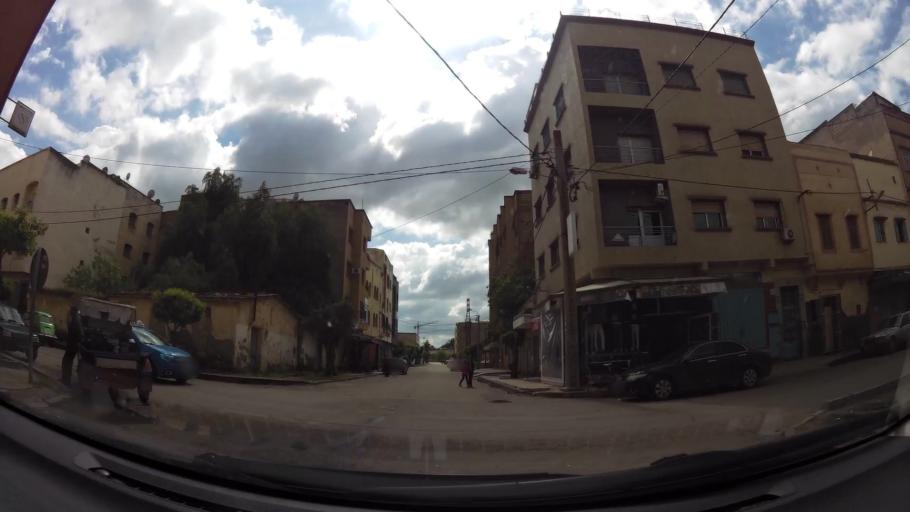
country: MA
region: Chaouia-Ouardigha
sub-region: Settat Province
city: Berrechid
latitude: 33.2686
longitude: -7.5875
